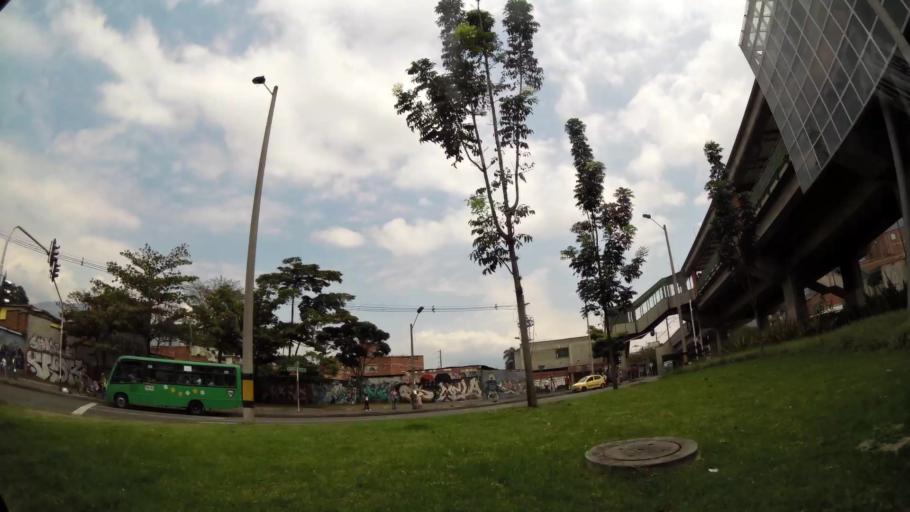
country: CO
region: Antioquia
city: Medellin
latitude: 6.2625
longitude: -75.5645
